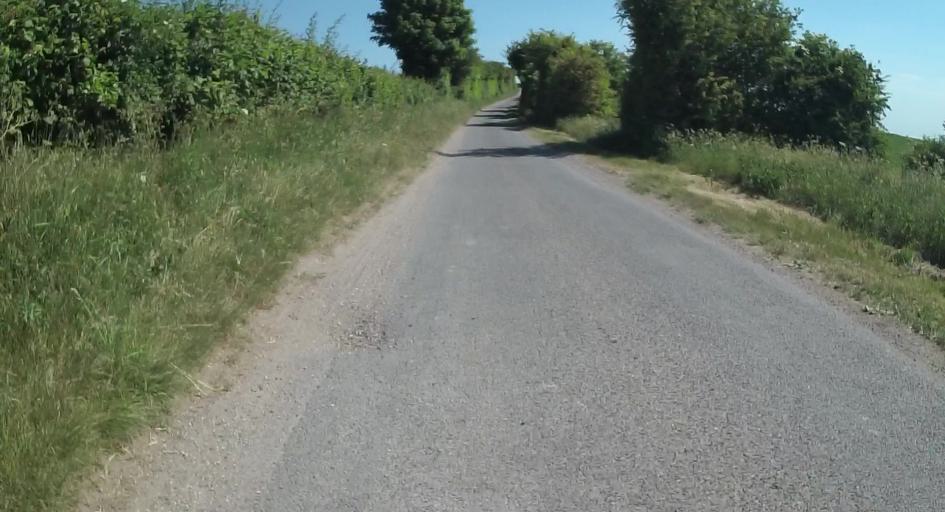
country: GB
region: England
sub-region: Hampshire
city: Kingsclere
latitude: 51.3054
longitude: -1.2957
